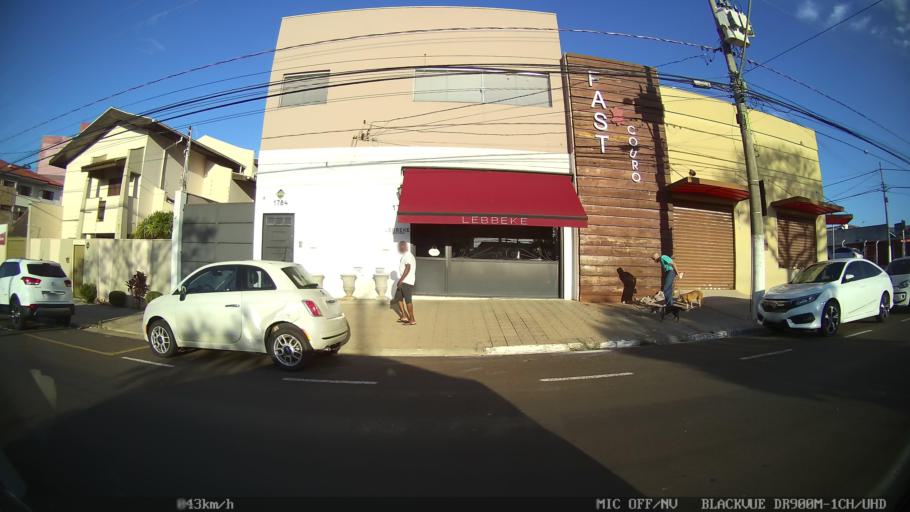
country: BR
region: Sao Paulo
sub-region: Franca
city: Franca
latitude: -20.5220
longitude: -47.3859
